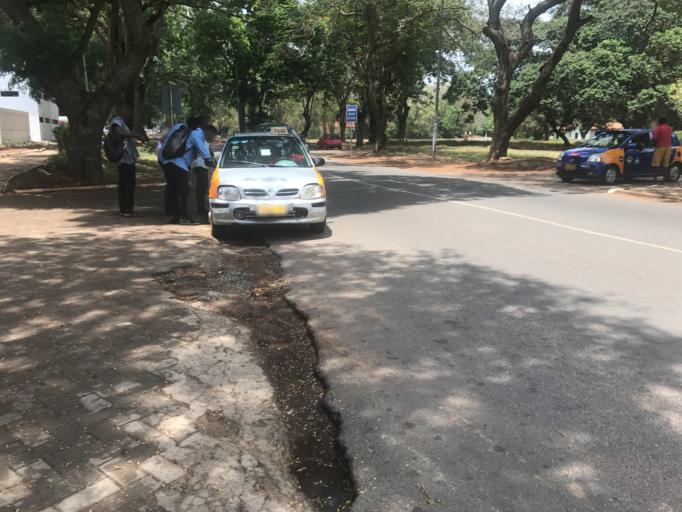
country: GH
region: Greater Accra
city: Medina Estates
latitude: 5.6445
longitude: -0.1851
